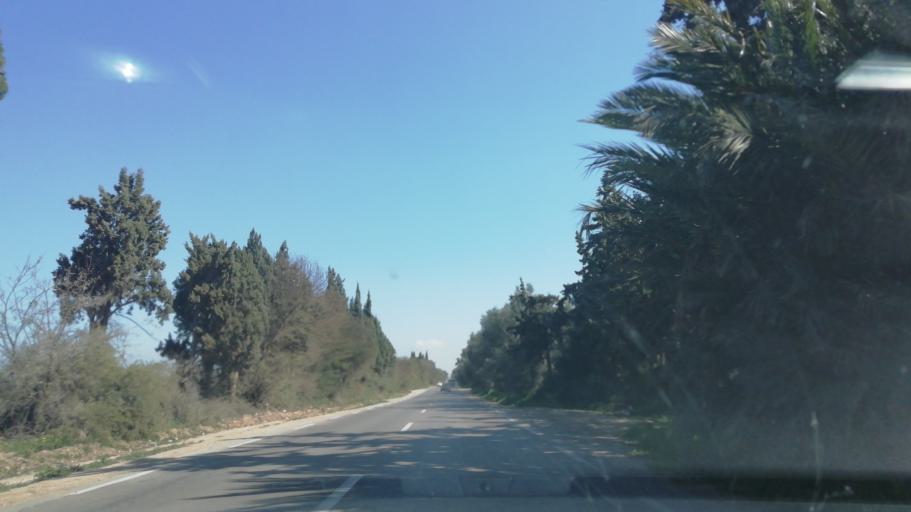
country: DZ
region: Mascara
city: Sig
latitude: 35.5737
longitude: -0.0146
